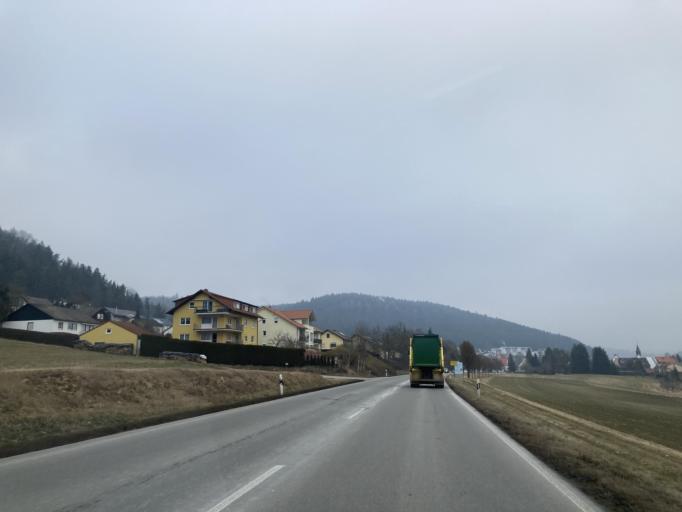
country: DE
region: Baden-Wuerttemberg
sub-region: Freiburg Region
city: Immendingen
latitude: 47.9334
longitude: 8.7036
